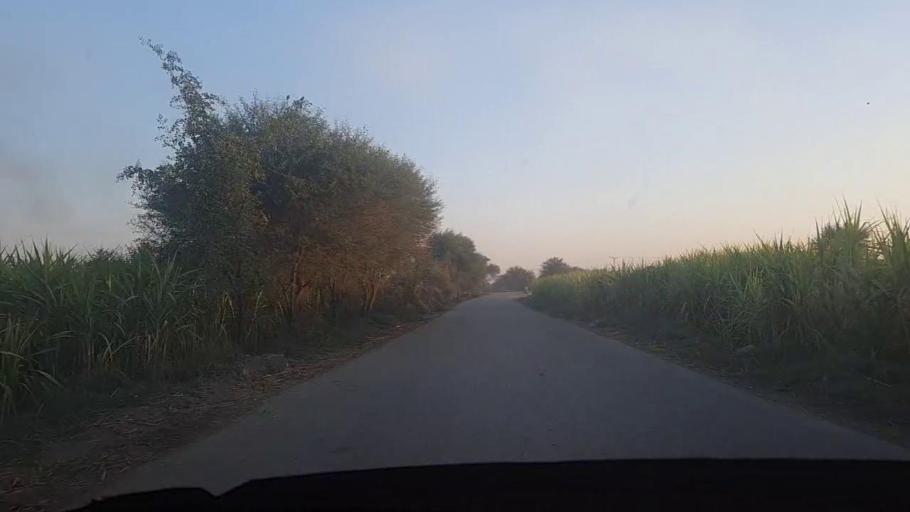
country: PK
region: Sindh
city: Sobhadero
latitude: 27.3420
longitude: 68.3783
